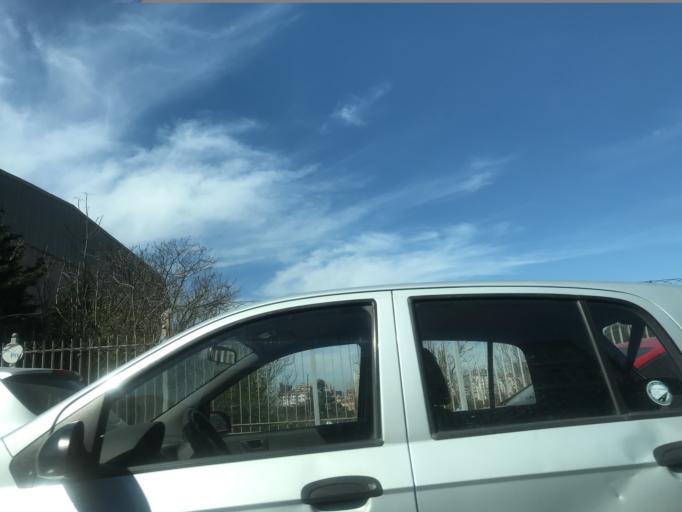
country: TR
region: Istanbul
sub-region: Atasehir
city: Atasehir
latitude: 40.9706
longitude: 29.1081
